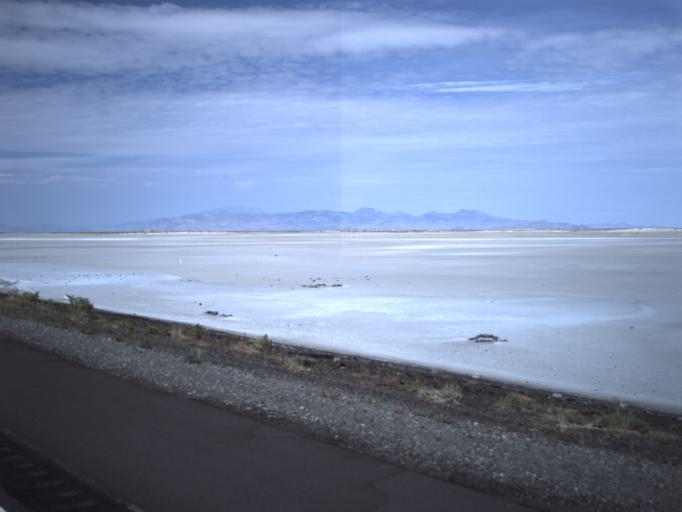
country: US
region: Utah
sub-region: Tooele County
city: Wendover
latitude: 40.7304
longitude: -113.4415
